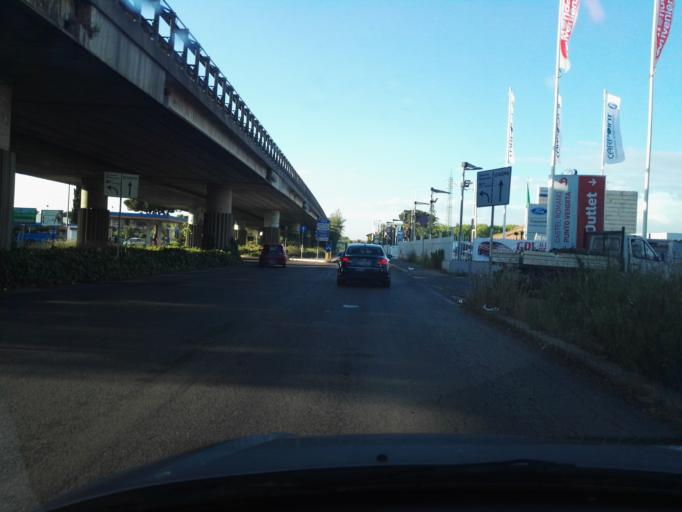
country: IT
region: Latium
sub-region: Citta metropolitana di Roma Capitale
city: Selcetta
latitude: 41.7925
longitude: 12.4520
